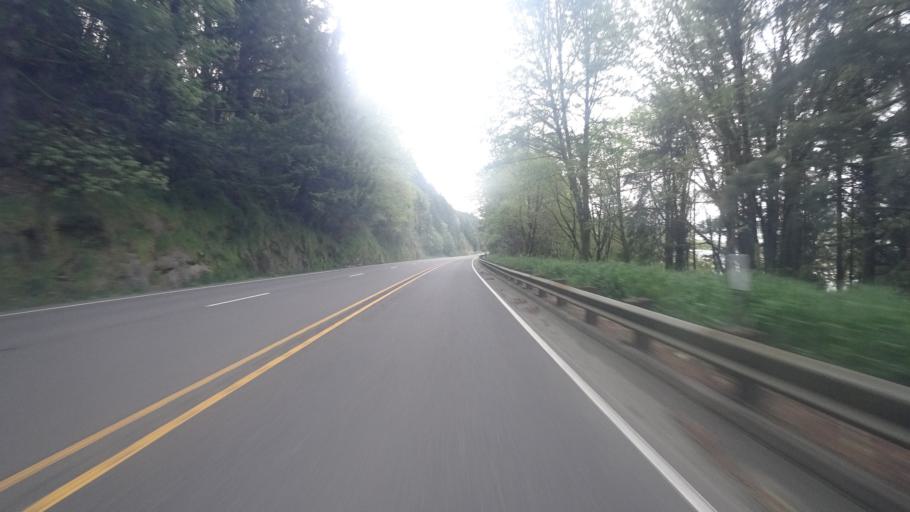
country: US
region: Oregon
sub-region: Douglas County
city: Reedsport
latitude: 43.7489
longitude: -124.1196
